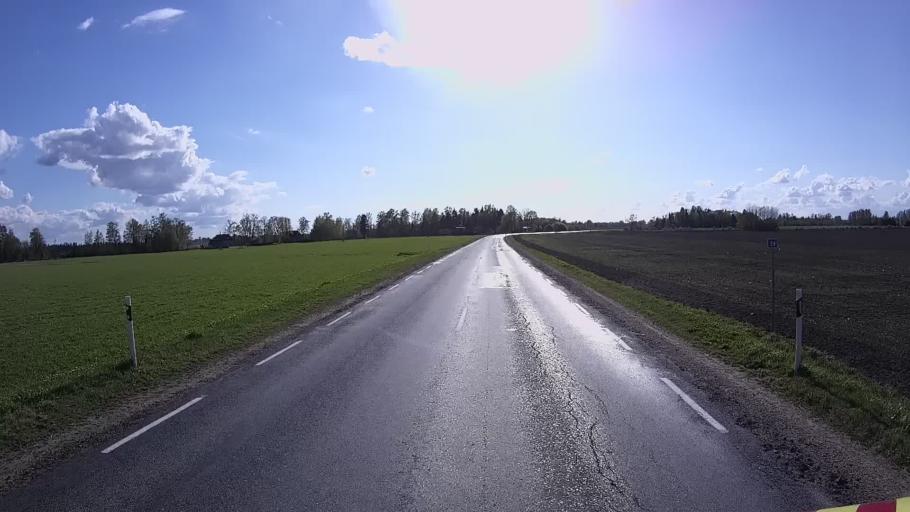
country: EE
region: Viljandimaa
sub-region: Vohma linn
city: Vohma
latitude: 58.6399
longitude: 25.6714
